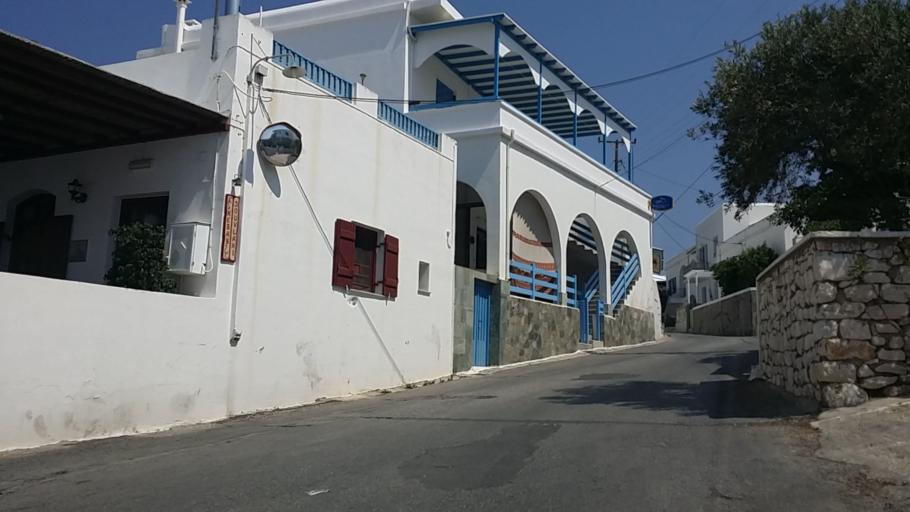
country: GR
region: South Aegean
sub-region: Nomos Kykladon
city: Naousa
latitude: 37.0431
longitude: 25.2495
